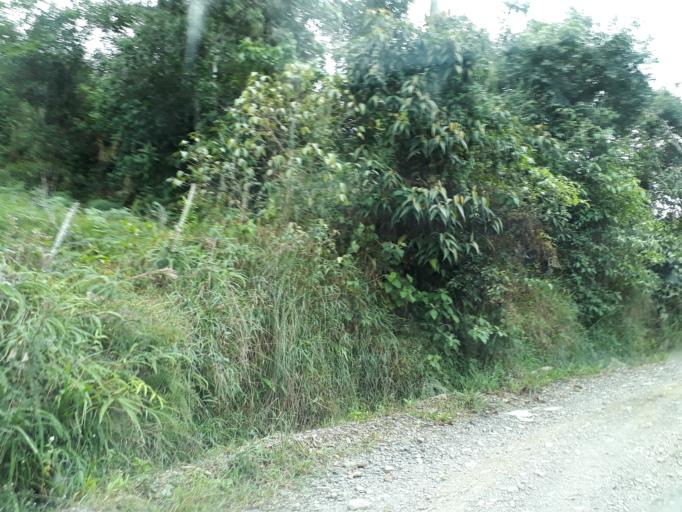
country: CO
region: Boyaca
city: Muzo
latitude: 5.3846
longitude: -74.1027
